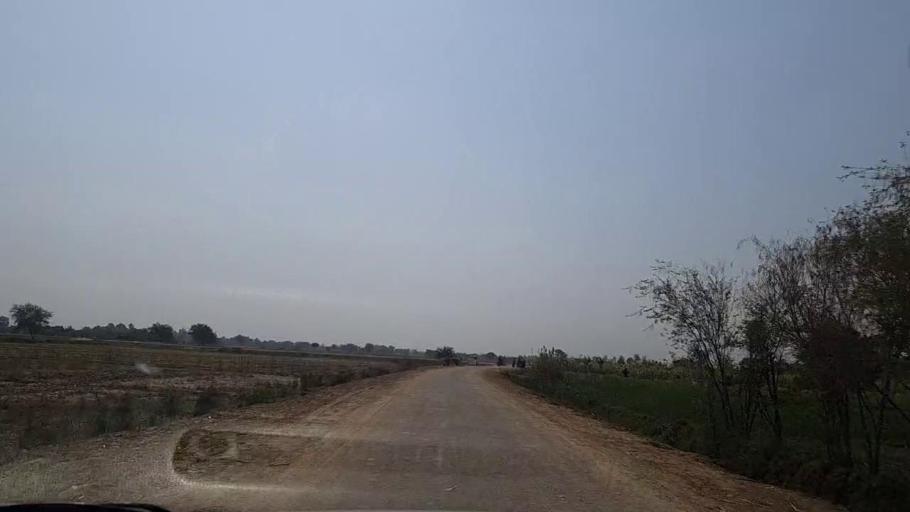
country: PK
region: Sindh
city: Mirpur Khas
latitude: 25.4841
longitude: 69.1939
